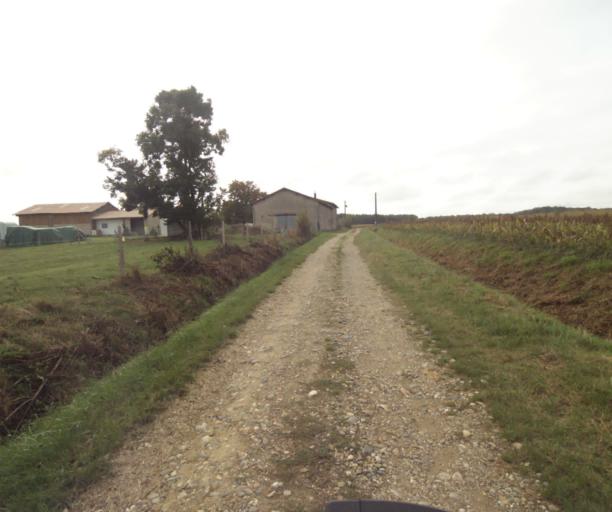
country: FR
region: Midi-Pyrenees
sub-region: Departement du Tarn-et-Garonne
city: Campsas
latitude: 43.9212
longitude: 1.2964
